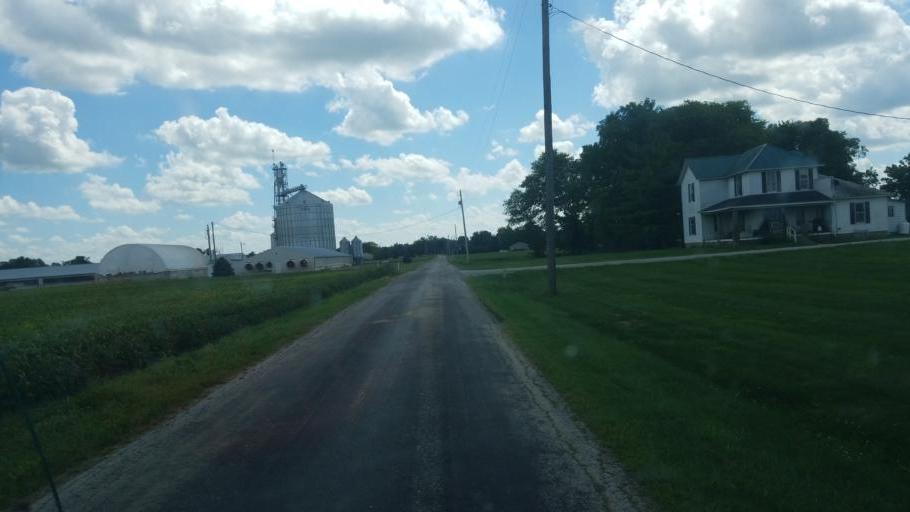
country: US
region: Ohio
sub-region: Marion County
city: Prospect
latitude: 40.4614
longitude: -83.1684
